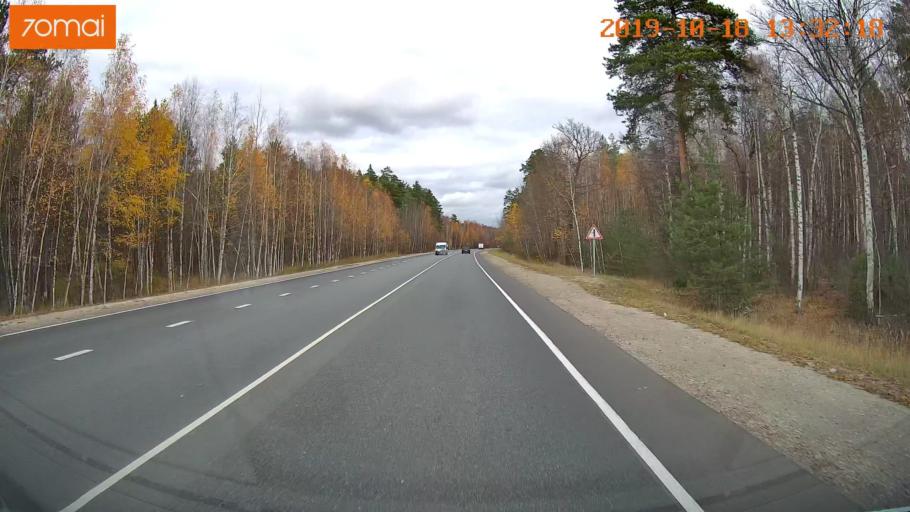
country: RU
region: Rjazan
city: Solotcha
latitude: 54.8314
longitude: 39.9167
